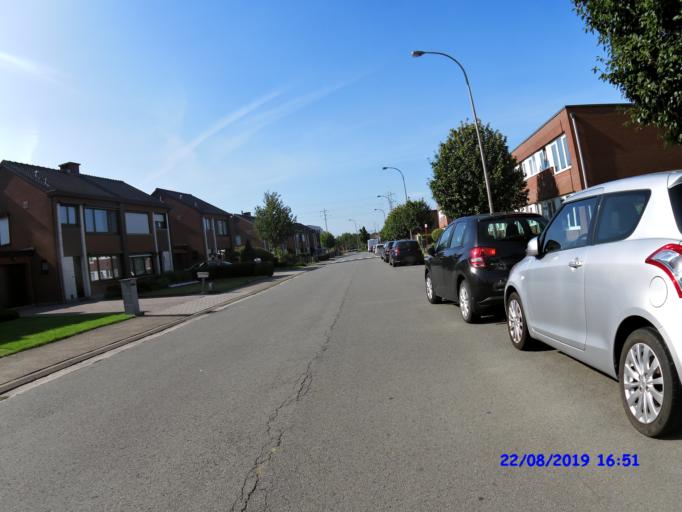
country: BE
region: Flanders
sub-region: Provincie Oost-Vlaanderen
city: Sint-Niklaas
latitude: 51.1569
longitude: 4.1441
